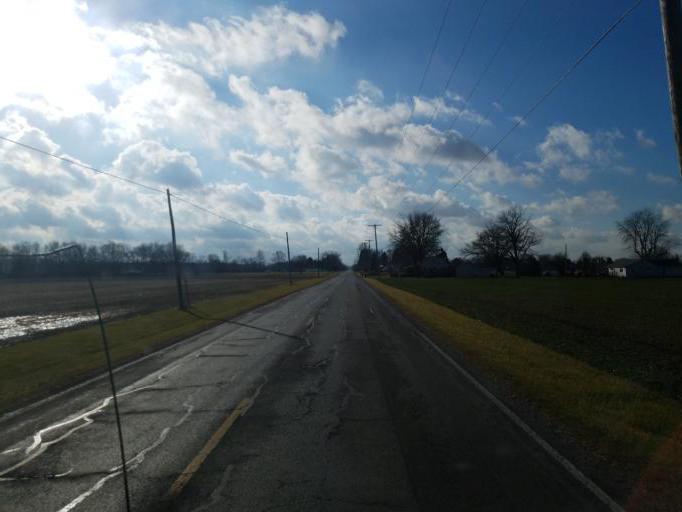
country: US
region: Ohio
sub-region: Marion County
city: Marion
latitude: 40.5765
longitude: -83.1644
